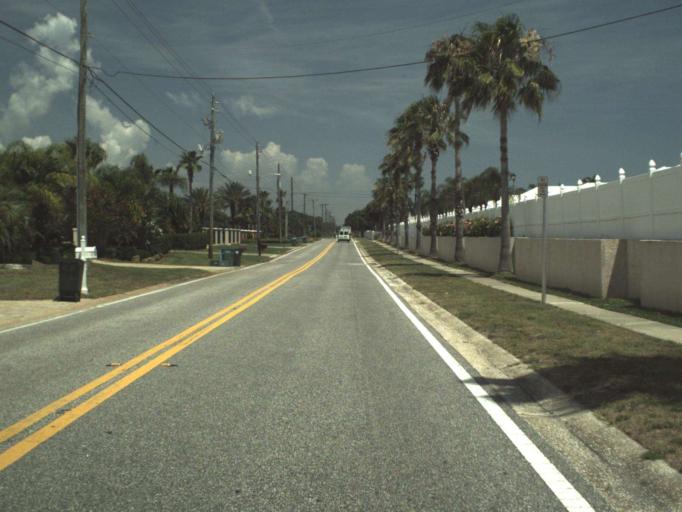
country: US
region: Florida
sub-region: Volusia County
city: Daytona Beach Shores
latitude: 29.1800
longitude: -80.9884
